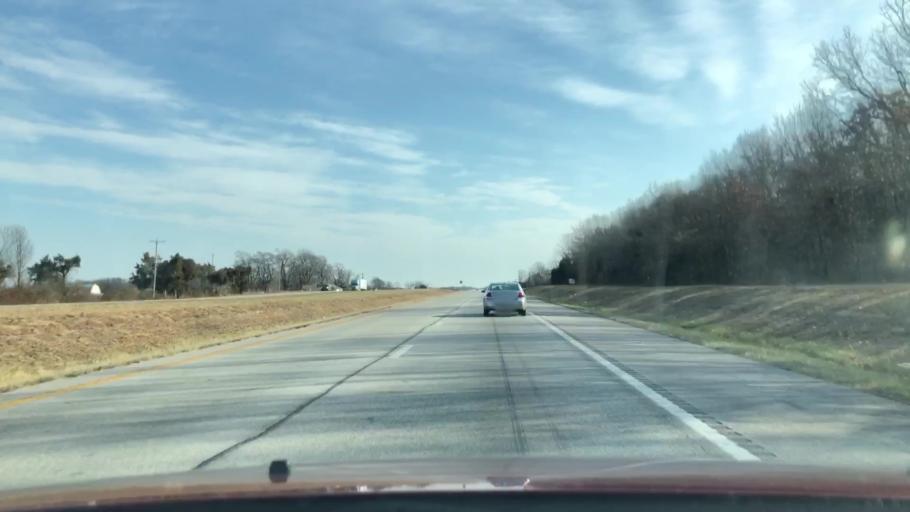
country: US
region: Missouri
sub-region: Christian County
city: Ozark
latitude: 37.1196
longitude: -93.1682
